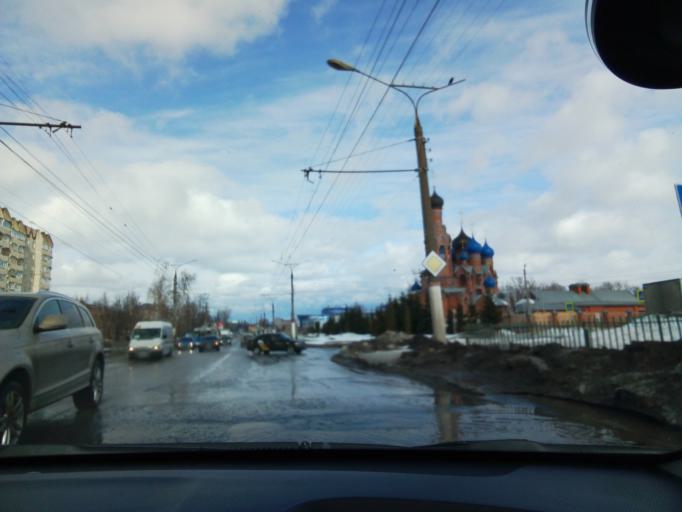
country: RU
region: Chuvashia
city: Novyye Lapsary
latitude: 56.1179
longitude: 47.1940
